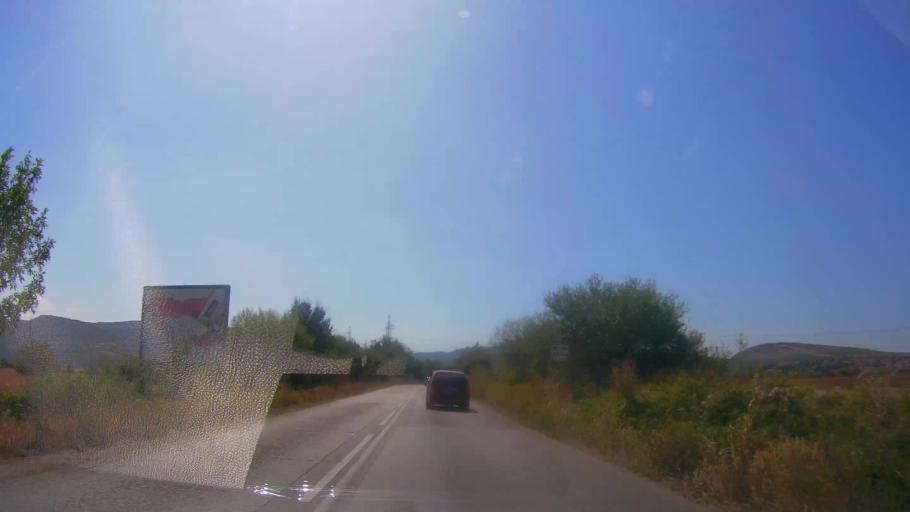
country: BG
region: Veliko Turnovo
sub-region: Obshtina Gorna Oryakhovitsa
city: Purvomaytsi
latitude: 43.1544
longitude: 25.6184
